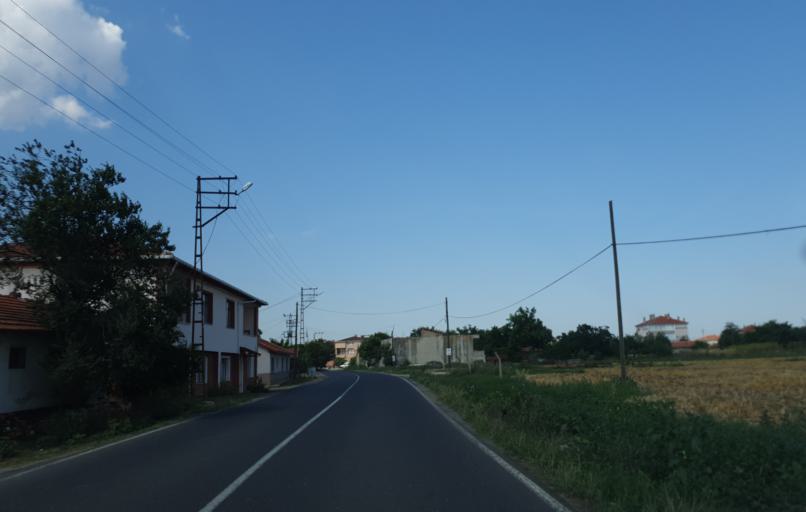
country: TR
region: Tekirdag
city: Muratli
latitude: 41.2173
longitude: 27.5415
